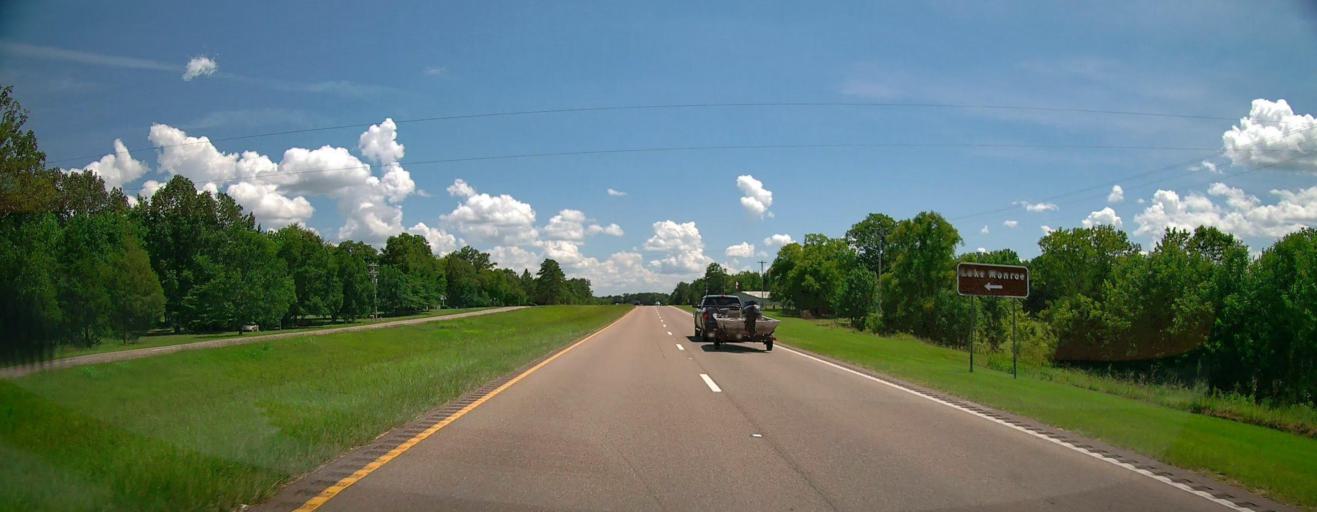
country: US
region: Mississippi
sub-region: Lee County
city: Nettleton
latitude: 33.9748
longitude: -88.6140
